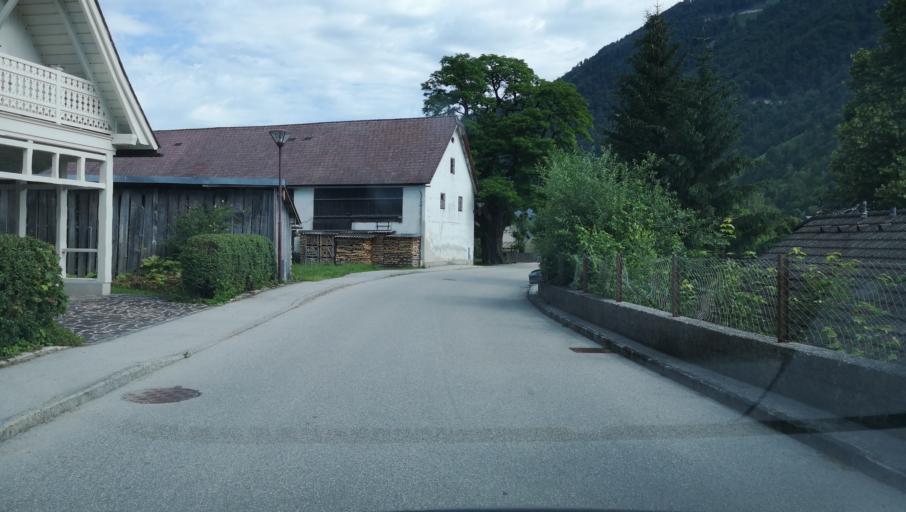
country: AT
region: Lower Austria
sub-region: Politischer Bezirk Amstetten
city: Hollenstein an der Ybbs
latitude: 47.8008
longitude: 14.7709
